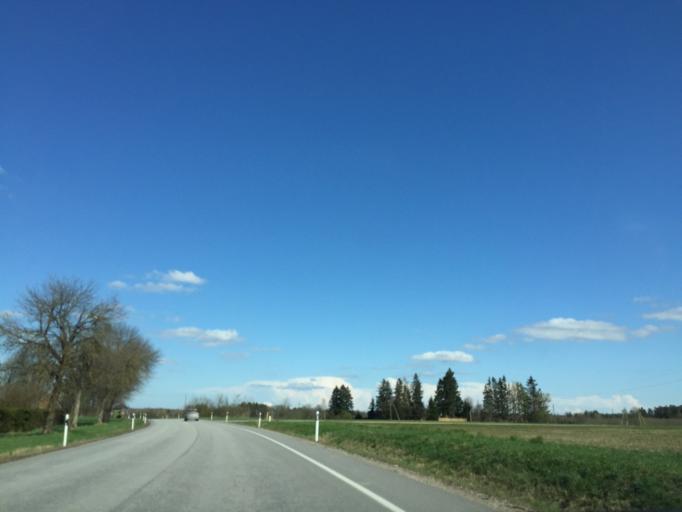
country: EE
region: Valgamaa
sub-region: Valga linn
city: Valga
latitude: 57.8625
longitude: 26.2163
